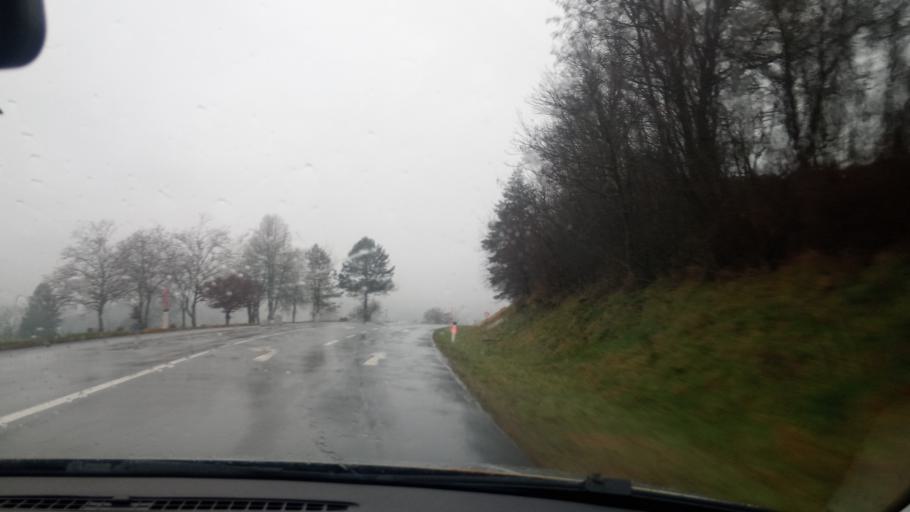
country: AT
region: Carinthia
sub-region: Politischer Bezirk Klagenfurt Land
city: Keutschach am See
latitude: 46.5894
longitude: 14.1751
